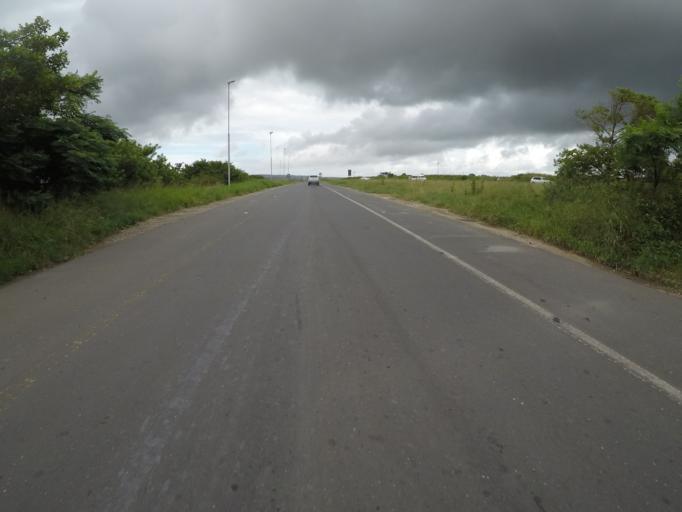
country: ZA
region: KwaZulu-Natal
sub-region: uThungulu District Municipality
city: eSikhawini
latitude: -28.8157
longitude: 31.9139
